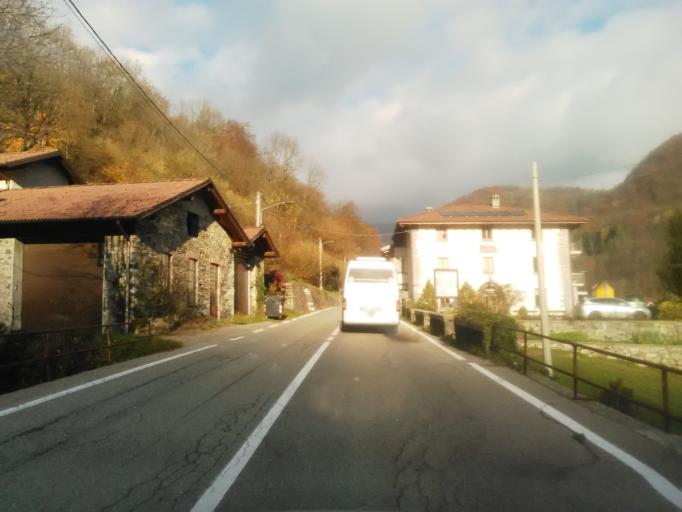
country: IT
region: Piedmont
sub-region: Provincia di Vercelli
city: Varallo
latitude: 45.8270
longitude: 8.2502
